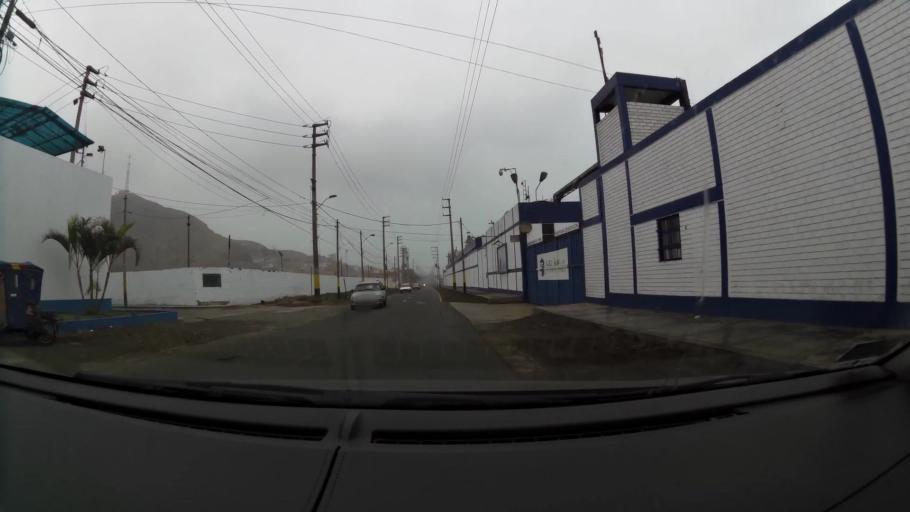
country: PE
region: Lima
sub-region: Provincia de Huaral
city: Chancay
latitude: -11.5791
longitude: -77.2693
